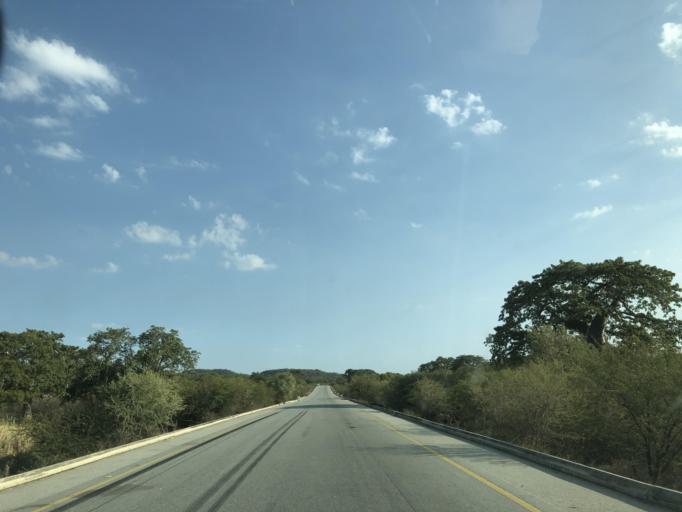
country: AO
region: Benguela
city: Benguela
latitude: -13.2362
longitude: 13.7709
